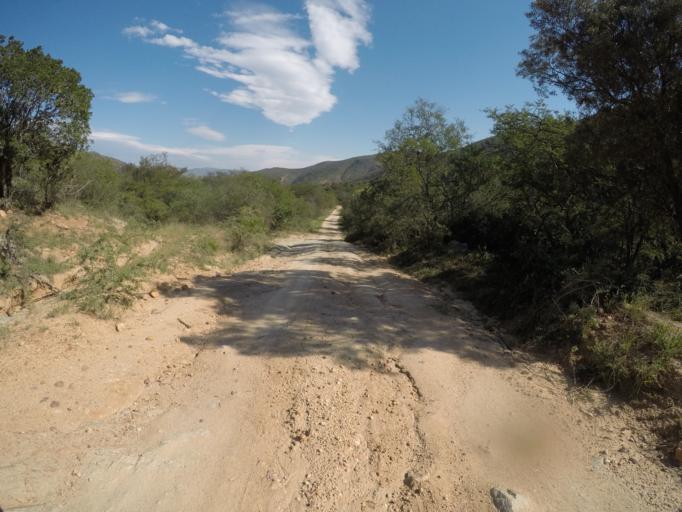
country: ZA
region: Eastern Cape
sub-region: Cacadu District Municipality
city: Kareedouw
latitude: -33.6446
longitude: 24.4589
